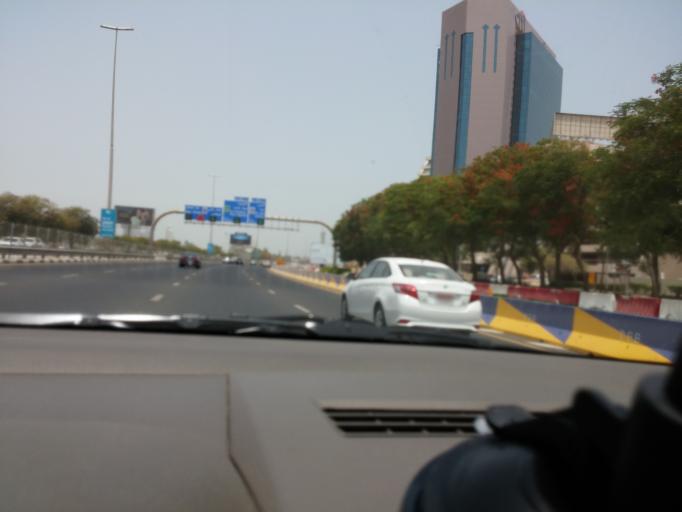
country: AE
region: Ash Shariqah
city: Sharjah
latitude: 25.2259
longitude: 55.3233
